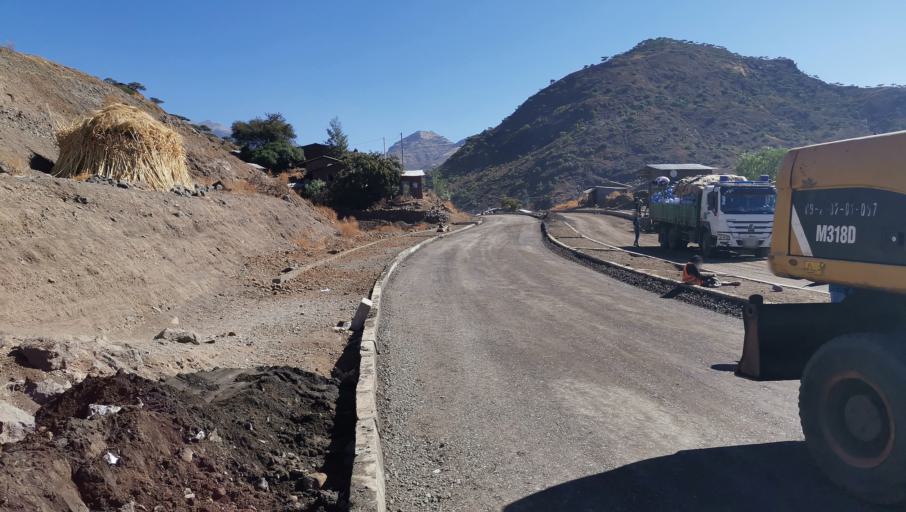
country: ET
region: Amhara
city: Lalibela
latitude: 12.2951
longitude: 38.9957
